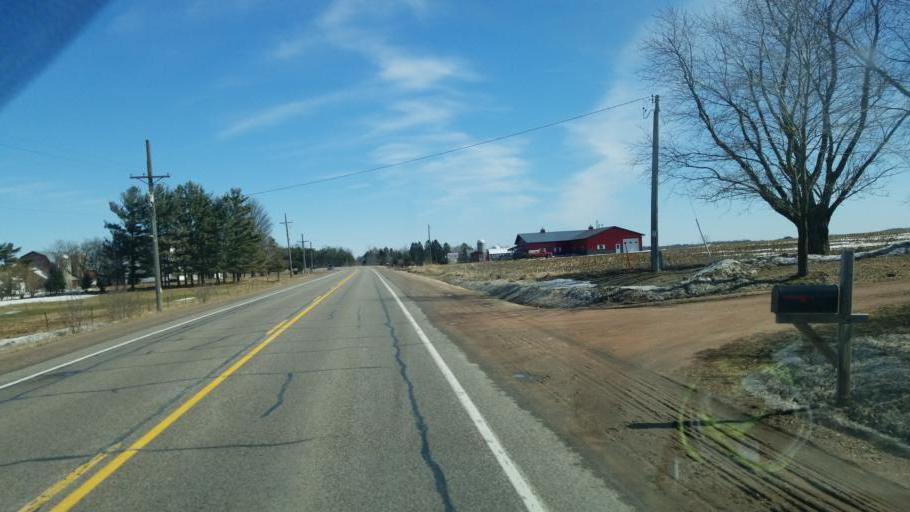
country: US
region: Wisconsin
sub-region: Clark County
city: Loyal
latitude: 44.5829
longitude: -90.3841
